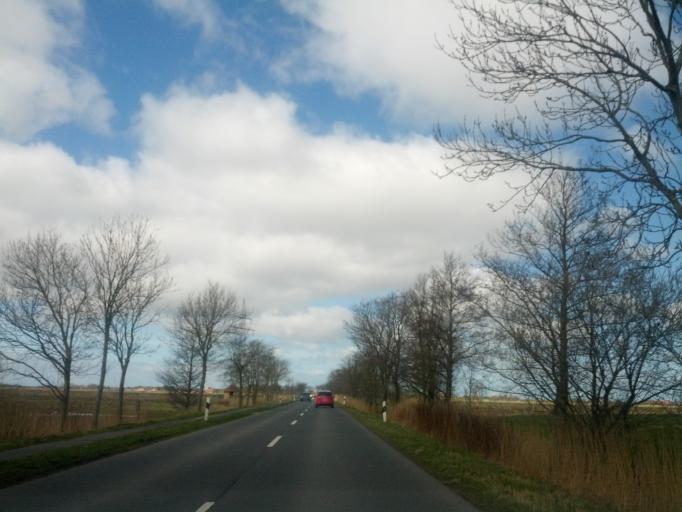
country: DE
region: Lower Saxony
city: Esens
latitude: 53.6632
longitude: 7.6007
